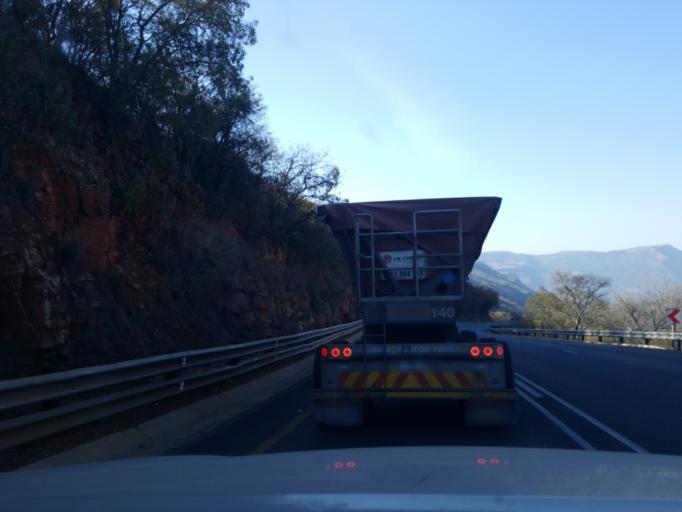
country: ZA
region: Mpumalanga
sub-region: Ehlanzeni District
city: Lydenburg
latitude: -25.4303
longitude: 30.4802
